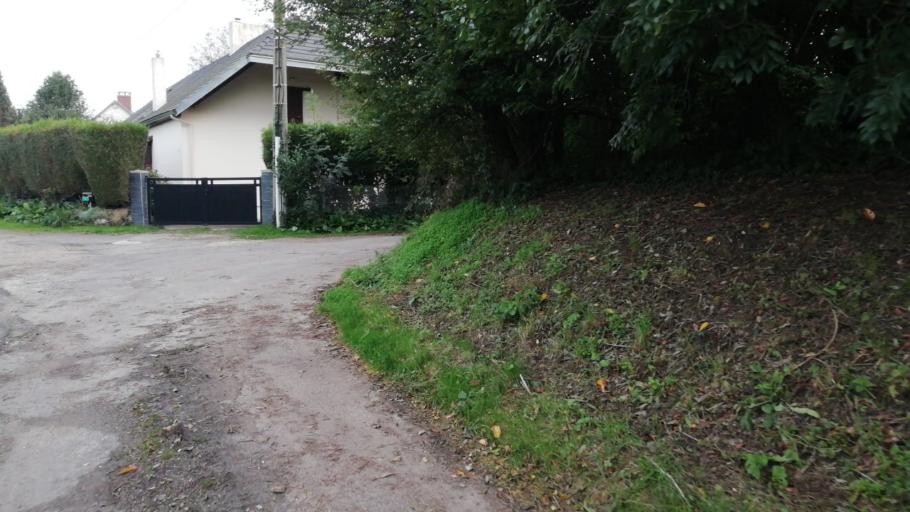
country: FR
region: Haute-Normandie
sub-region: Departement de la Seine-Maritime
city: Saint-Martin-du-Manoir
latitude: 49.5478
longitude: 0.2334
